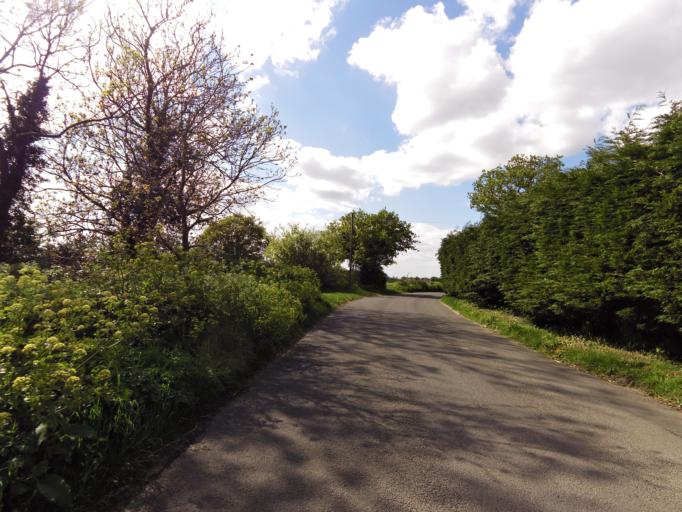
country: GB
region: England
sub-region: Suffolk
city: Kessingland
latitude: 52.4394
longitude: 1.6643
